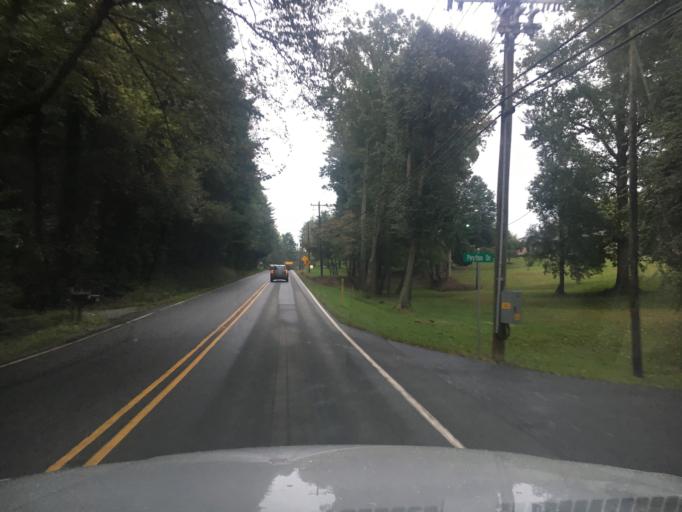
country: US
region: North Carolina
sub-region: Henderson County
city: Horse Shoe
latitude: 35.3393
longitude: -82.5361
